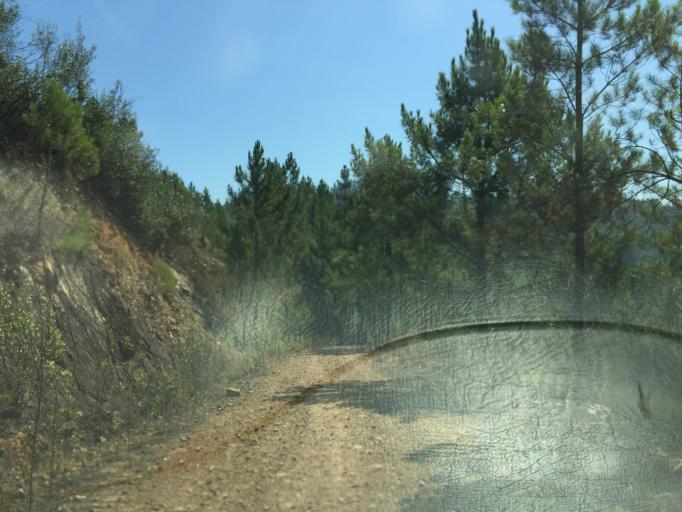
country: PT
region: Santarem
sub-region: Ferreira do Zezere
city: Ferreira do Zezere
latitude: 39.6522
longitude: -8.2379
